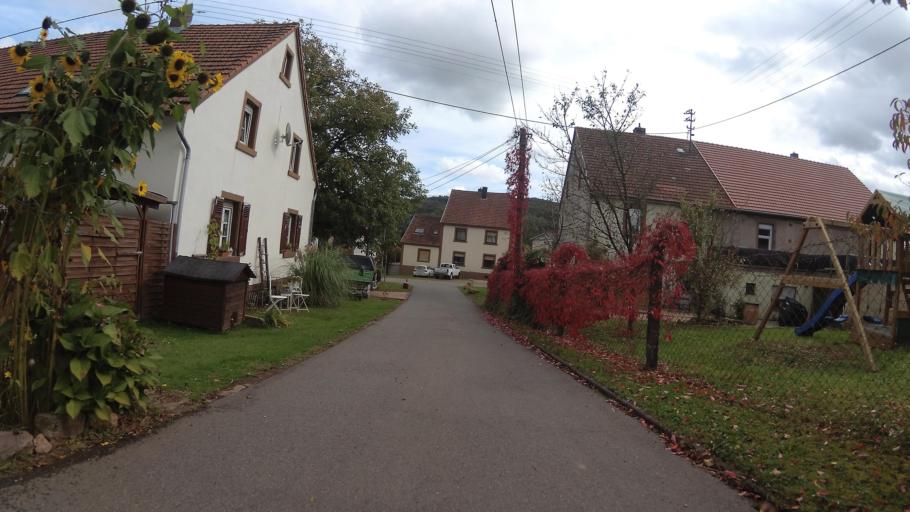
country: DE
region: Saarland
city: Namborn
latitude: 49.5260
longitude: 7.1628
